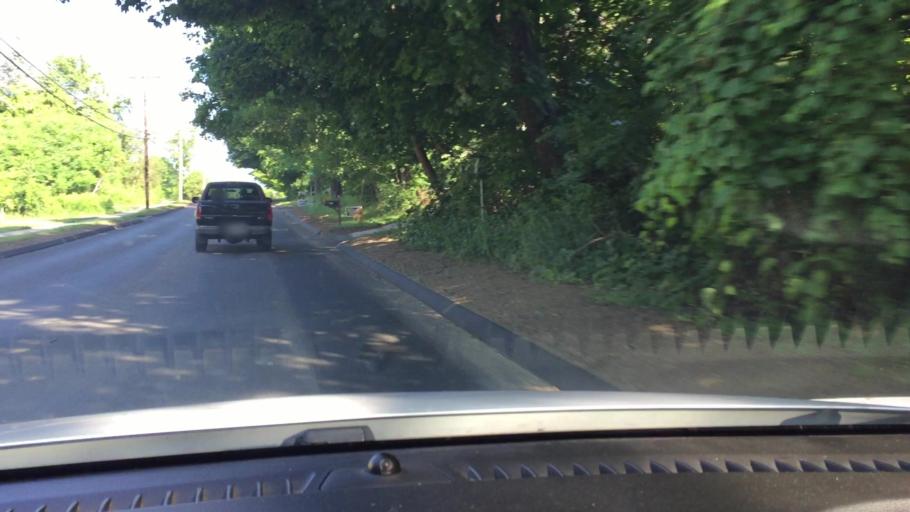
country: US
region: Massachusetts
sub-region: Berkshire County
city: Pittsfield
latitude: 42.4737
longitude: -73.2606
